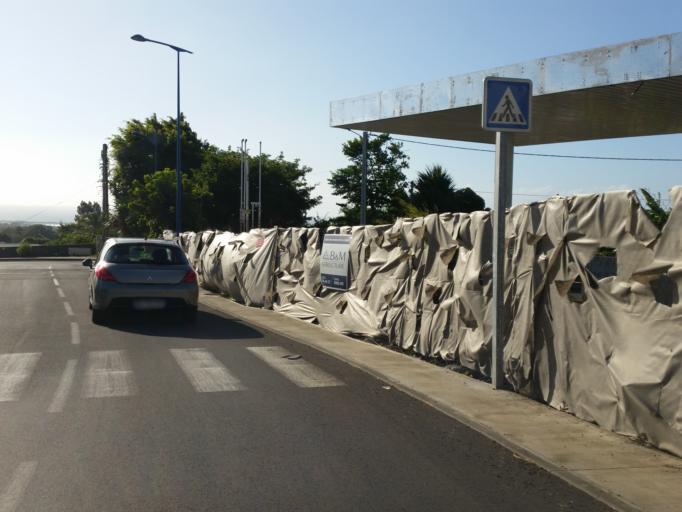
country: RE
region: Reunion
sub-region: Reunion
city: Sainte-Marie
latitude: -20.9178
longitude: 55.5144
